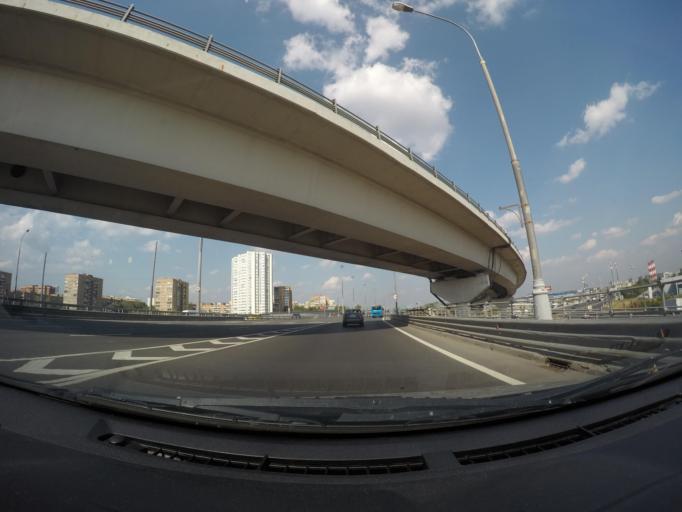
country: RU
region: Moskovskaya
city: Levoberezhnaya
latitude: 55.8861
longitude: 37.4825
